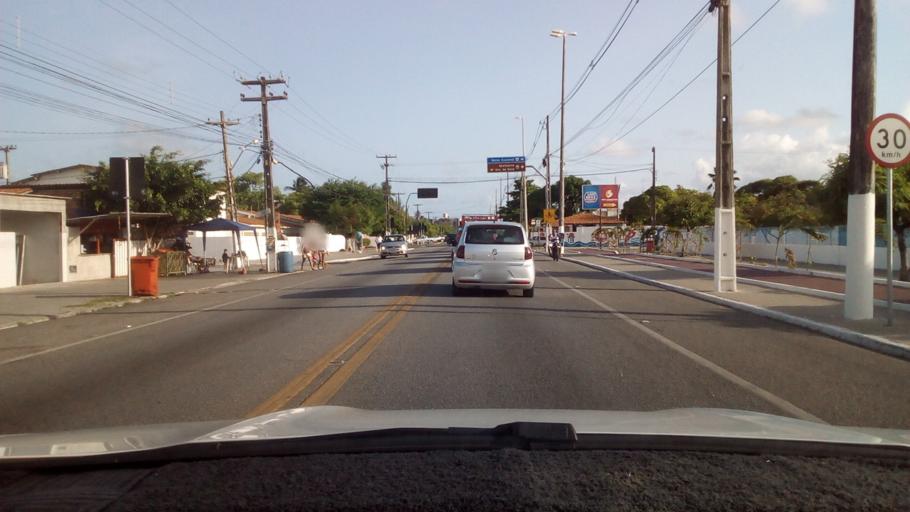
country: BR
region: Paraiba
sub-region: Cabedelo
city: Cabedelo
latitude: -6.9801
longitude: -34.8304
